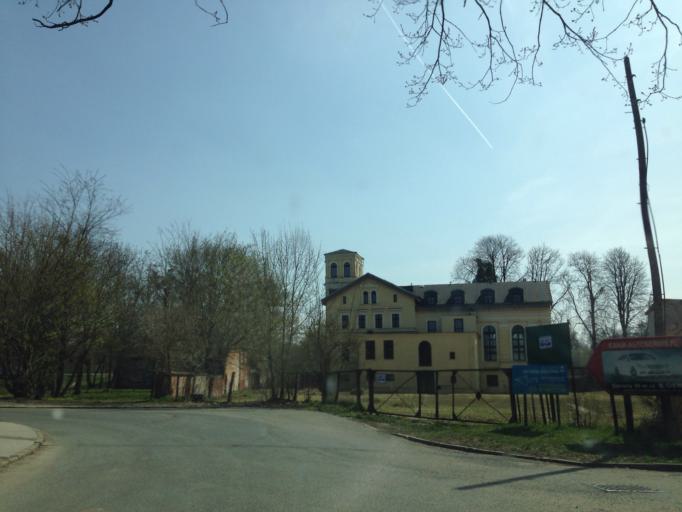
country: PL
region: Lower Silesian Voivodeship
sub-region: Powiat wroclawski
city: Wilczyce
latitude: 51.1007
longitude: 17.1179
